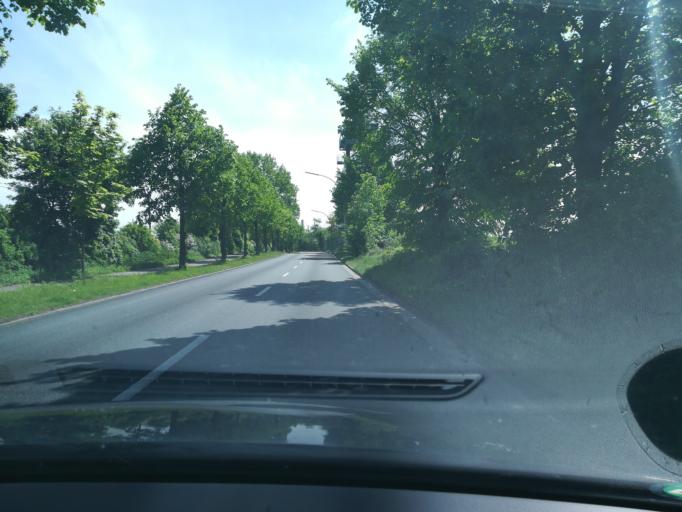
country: DE
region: Hamburg
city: Altona
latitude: 53.5038
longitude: 9.9447
